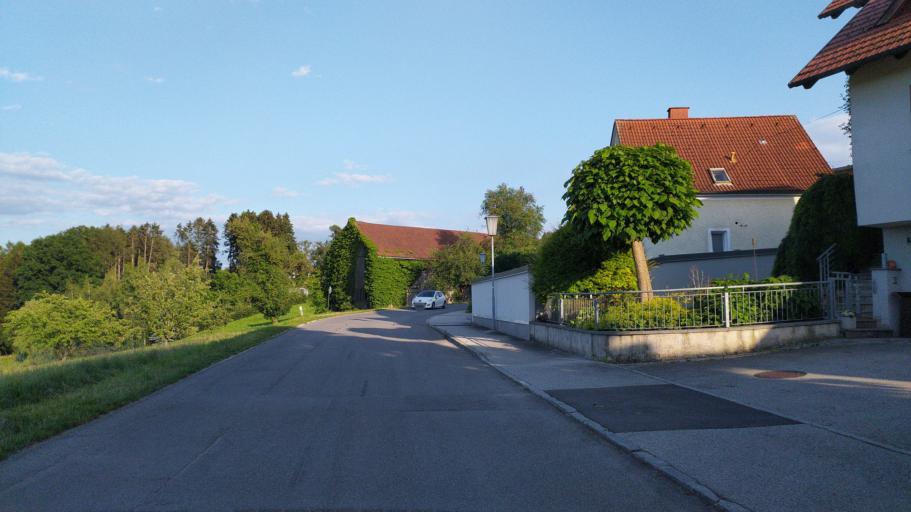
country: AT
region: Lower Austria
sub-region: Politischer Bezirk Amstetten
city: Strengberg
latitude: 48.1449
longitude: 14.6519
